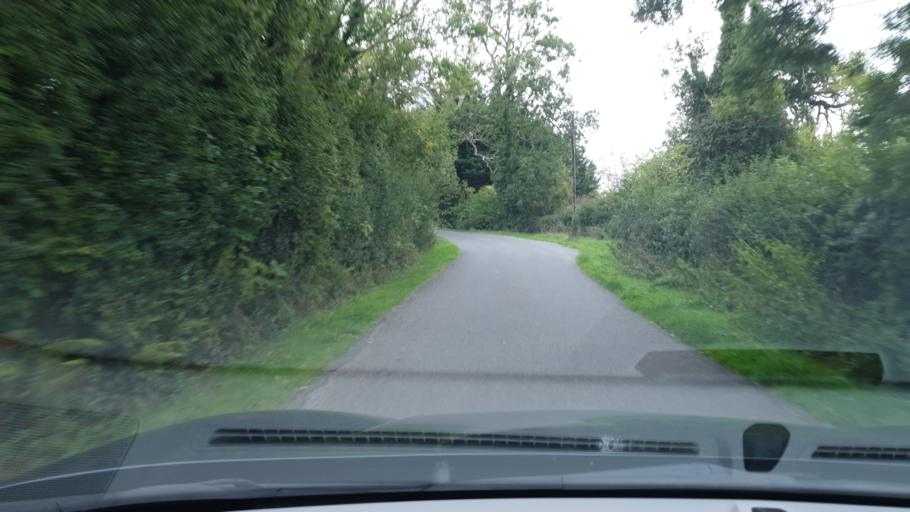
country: IE
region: Leinster
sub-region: An Mhi
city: Dunshaughlin
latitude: 53.4911
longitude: -6.5403
